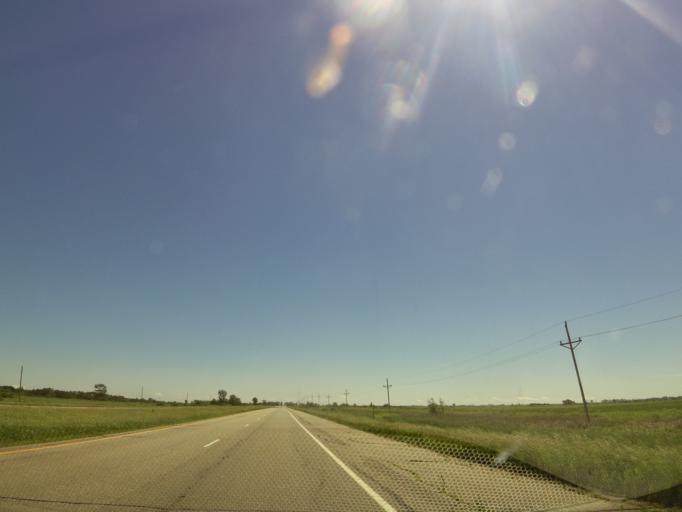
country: US
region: Minnesota
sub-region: Red Lake County
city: Red Lake Falls
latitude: 47.7601
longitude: -96.2973
